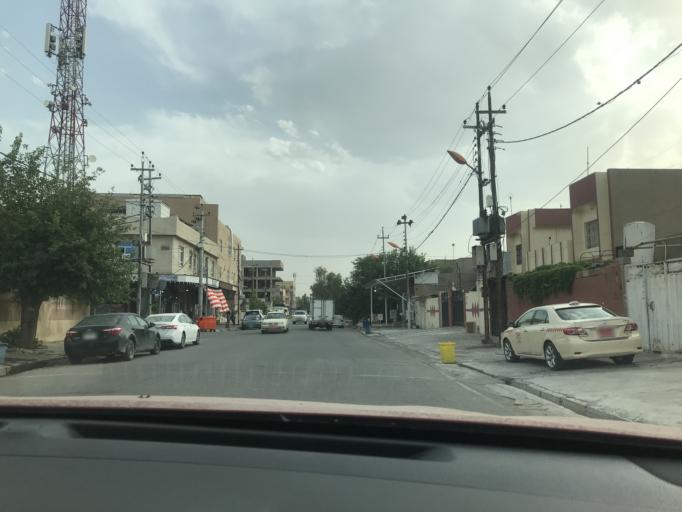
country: IQ
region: Arbil
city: Erbil
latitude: 36.1781
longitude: 43.9766
